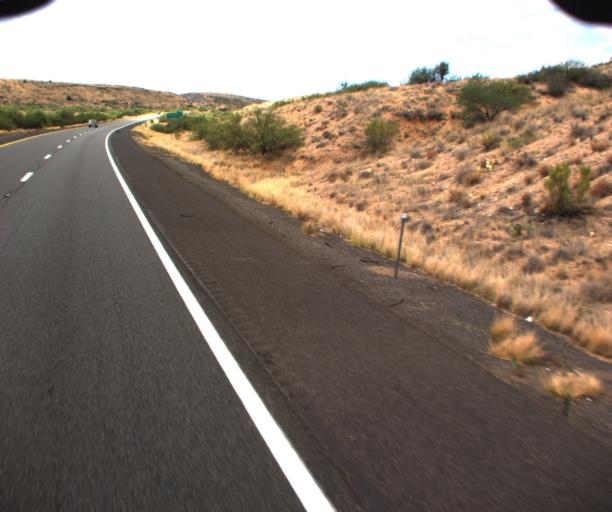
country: US
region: Arizona
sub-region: Yavapai County
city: Cordes Lakes
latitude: 34.2431
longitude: -112.1139
